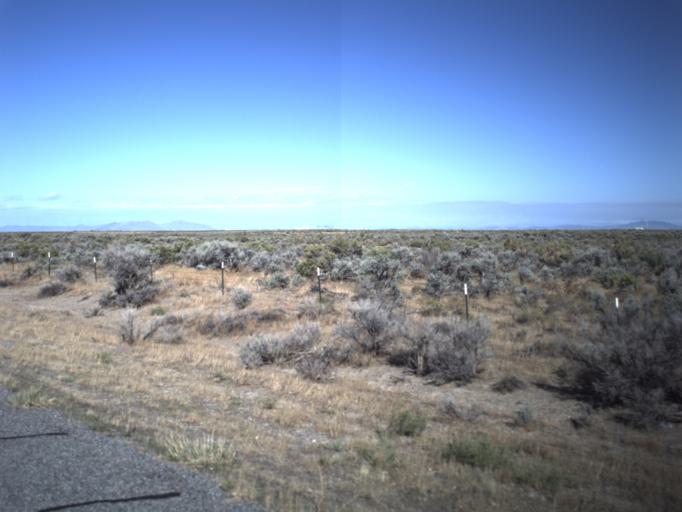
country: US
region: Utah
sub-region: Millard County
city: Delta
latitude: 39.3540
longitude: -112.4360
